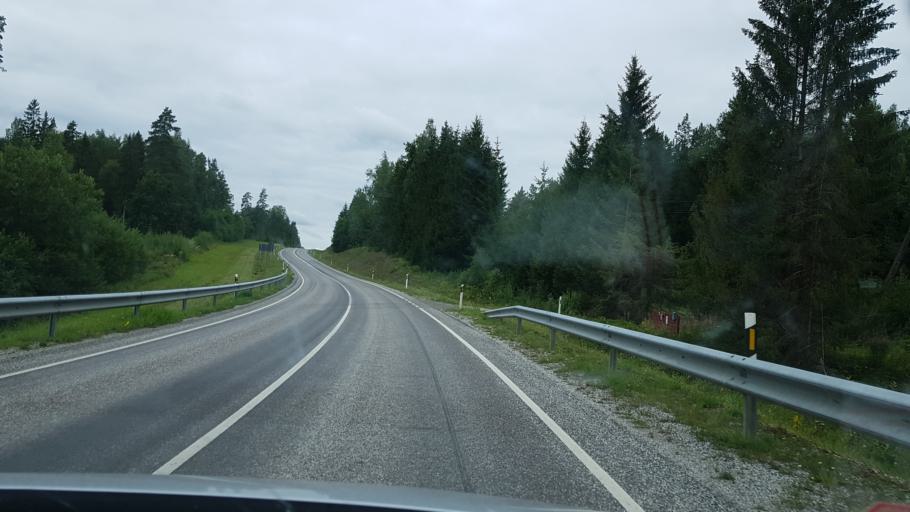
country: EE
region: Vorumaa
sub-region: Antsla vald
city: Vana-Antsla
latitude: 57.9978
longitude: 26.7227
